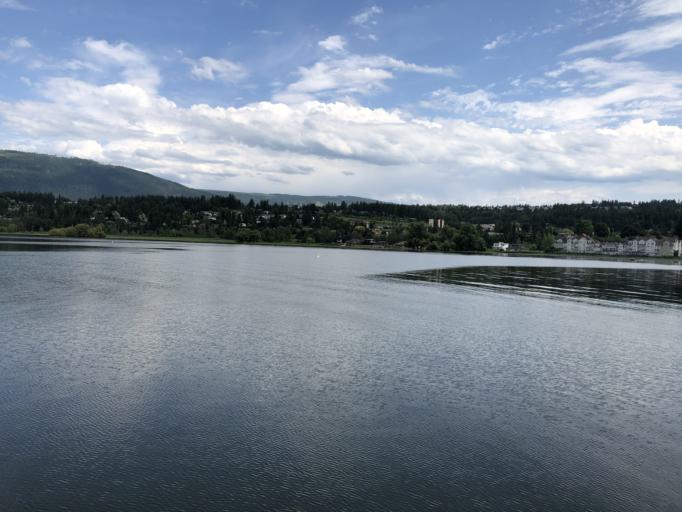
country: CA
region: British Columbia
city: Salmon Arm
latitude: 50.7094
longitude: -119.2834
